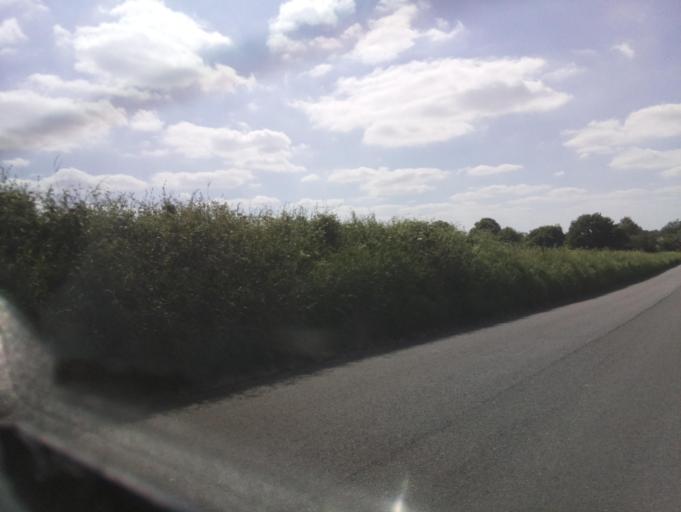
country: GB
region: England
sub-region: Wiltshire
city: Woodborough
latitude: 51.3594
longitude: -1.8397
